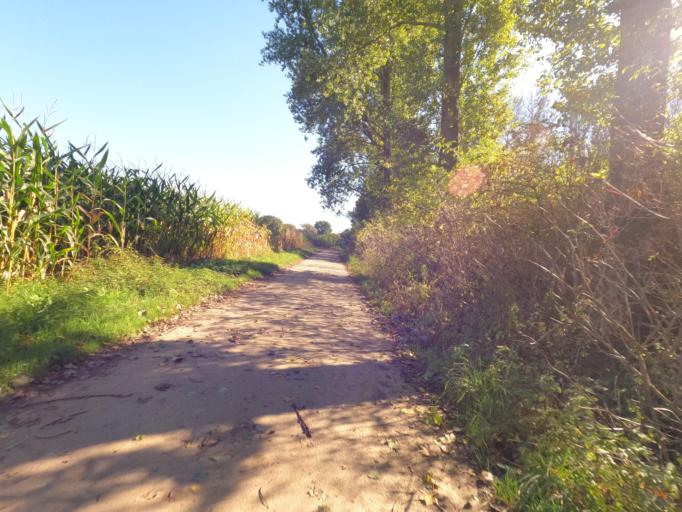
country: DE
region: North Rhine-Westphalia
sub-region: Regierungsbezirk Koln
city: Linnich
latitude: 51.0156
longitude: 6.2625
